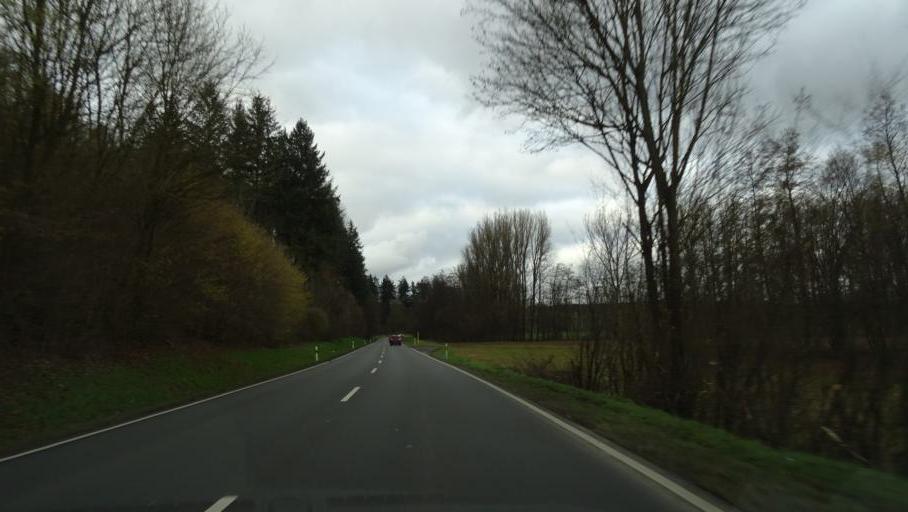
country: DE
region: Baden-Wuerttemberg
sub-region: Karlsruhe Region
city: Neckarbischofsheim
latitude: 49.3127
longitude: 8.9513
